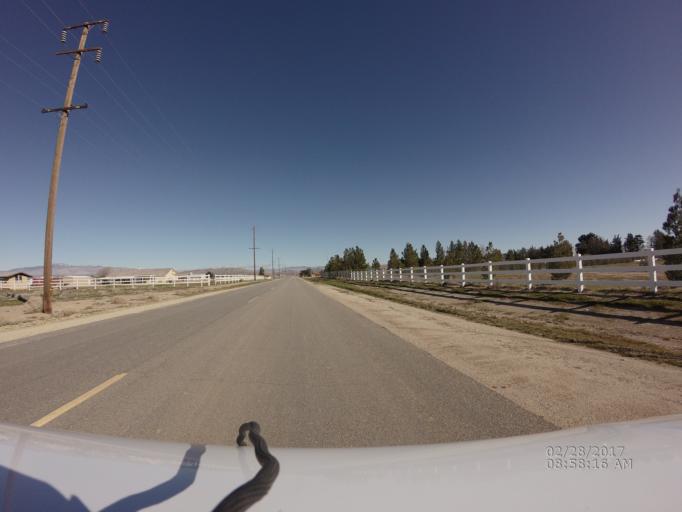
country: US
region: California
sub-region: Kern County
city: Rosamond
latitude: 34.8171
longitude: -118.2553
